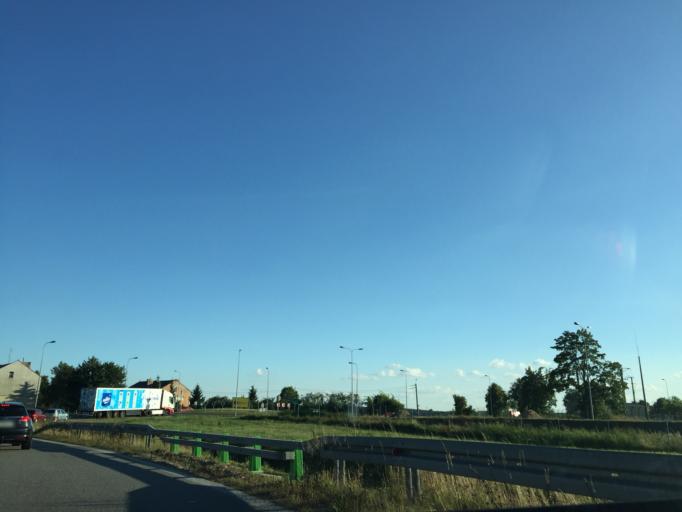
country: PL
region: Podlasie
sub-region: Powiat kolnenski
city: Stawiski
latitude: 53.3863
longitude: 22.1501
